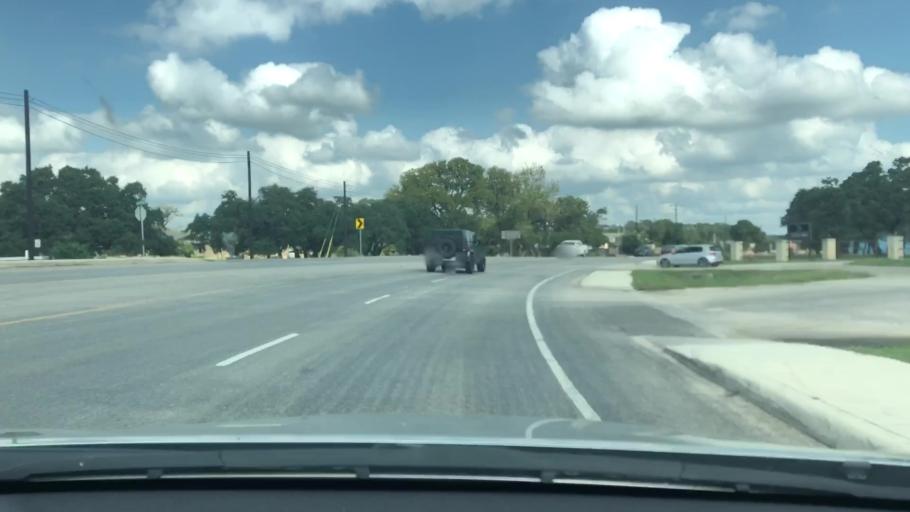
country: US
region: Texas
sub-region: Kendall County
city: Boerne
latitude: 29.7891
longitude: -98.7122
